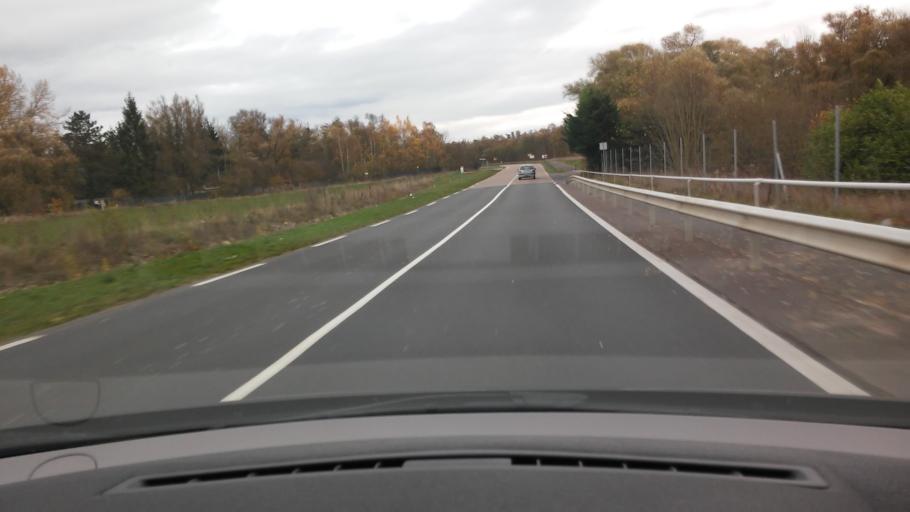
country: FR
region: Lorraine
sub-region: Departement de la Moselle
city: Ennery
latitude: 49.2243
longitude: 6.2001
